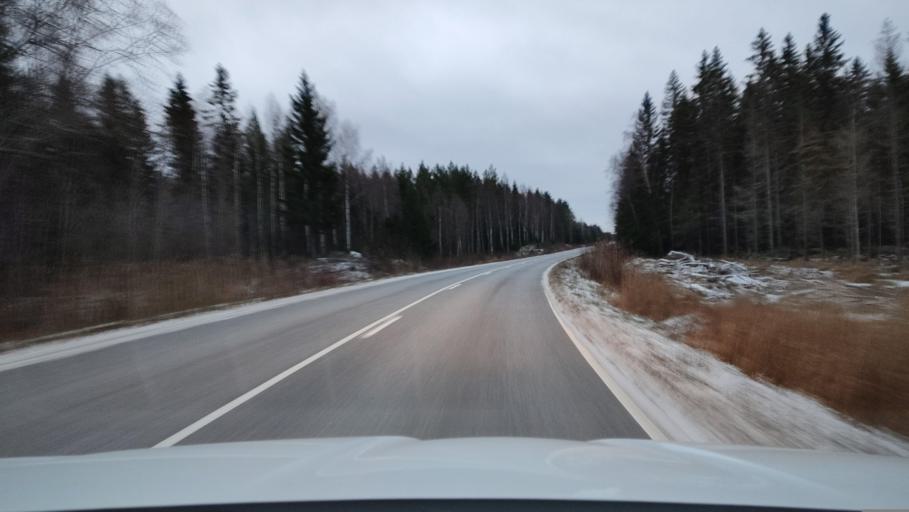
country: FI
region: Ostrobothnia
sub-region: Vaasa
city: Replot
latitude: 63.2646
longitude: 21.3577
